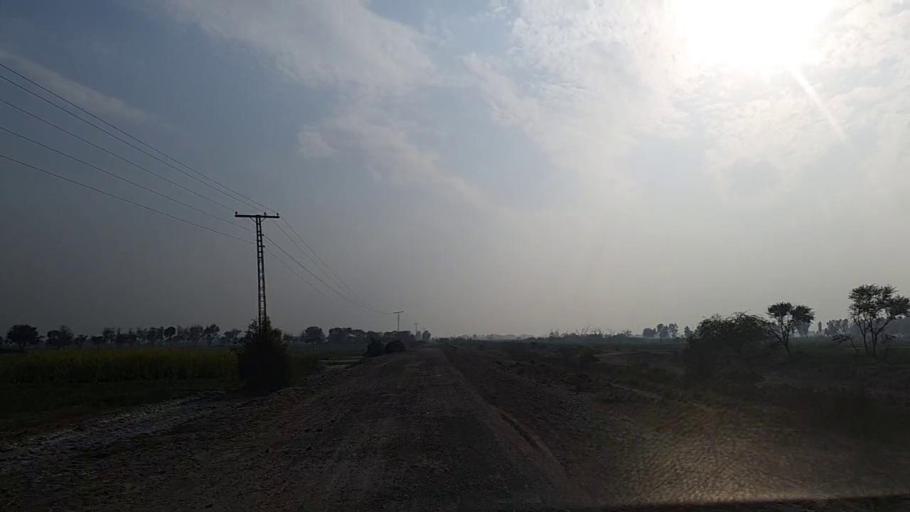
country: PK
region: Sindh
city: Jam Sahib
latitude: 26.3175
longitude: 68.5271
